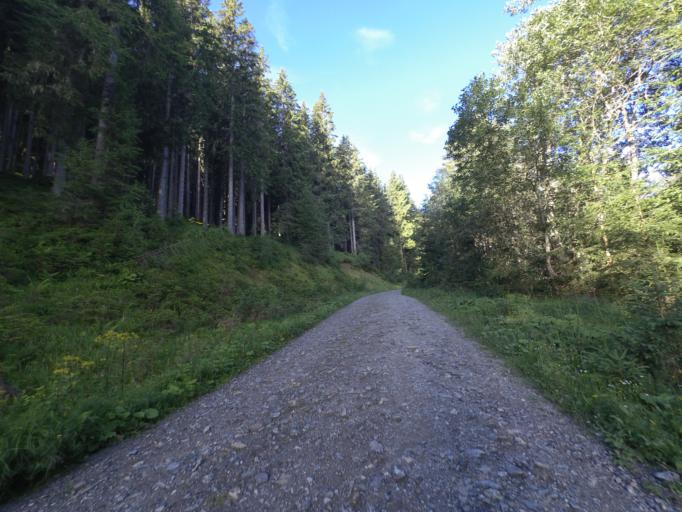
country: AT
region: Salzburg
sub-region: Politischer Bezirk Sankt Johann im Pongau
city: Goldegg
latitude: 47.3519
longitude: 13.0992
